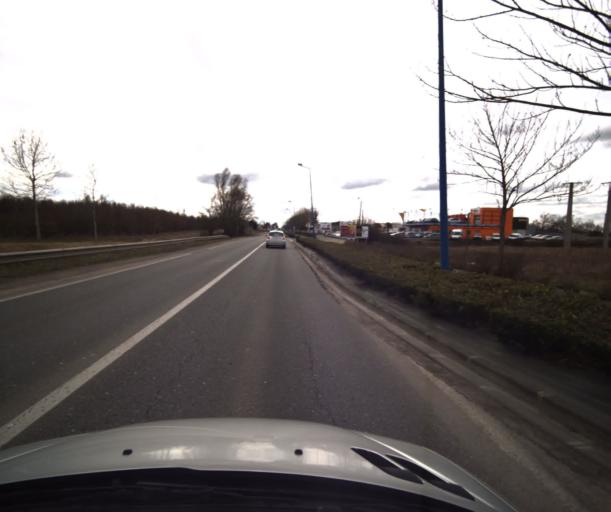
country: FR
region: Midi-Pyrenees
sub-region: Departement du Tarn-et-Garonne
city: Montauban
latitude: 44.0442
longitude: 1.3889
